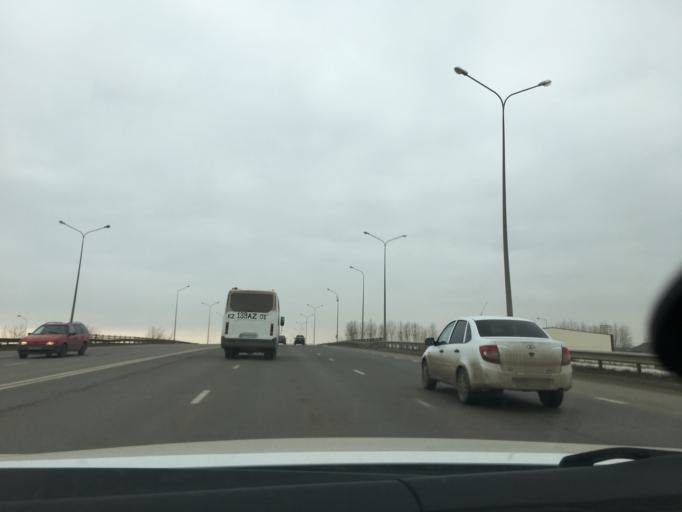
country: KZ
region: Astana Qalasy
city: Astana
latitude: 51.1410
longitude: 71.5252
